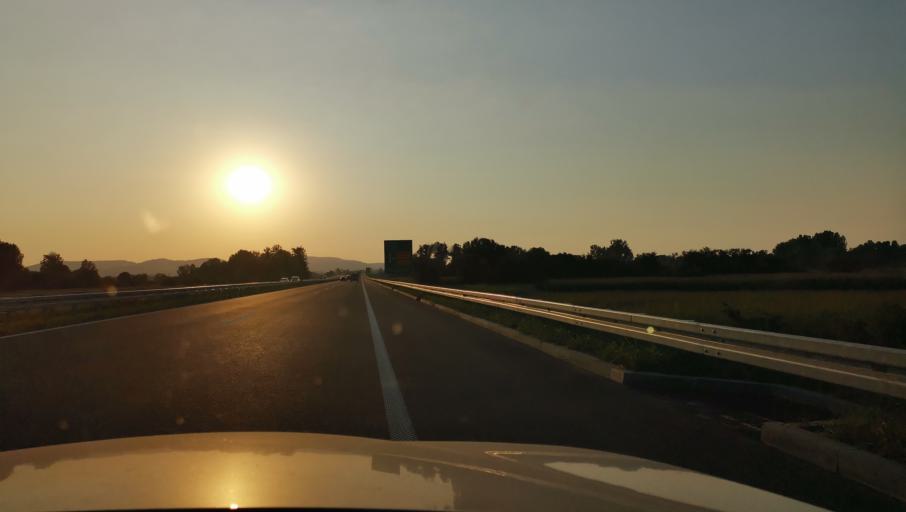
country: RS
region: Central Serbia
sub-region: Kolubarski Okrug
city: Lajkovac
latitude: 44.3530
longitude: 20.1473
